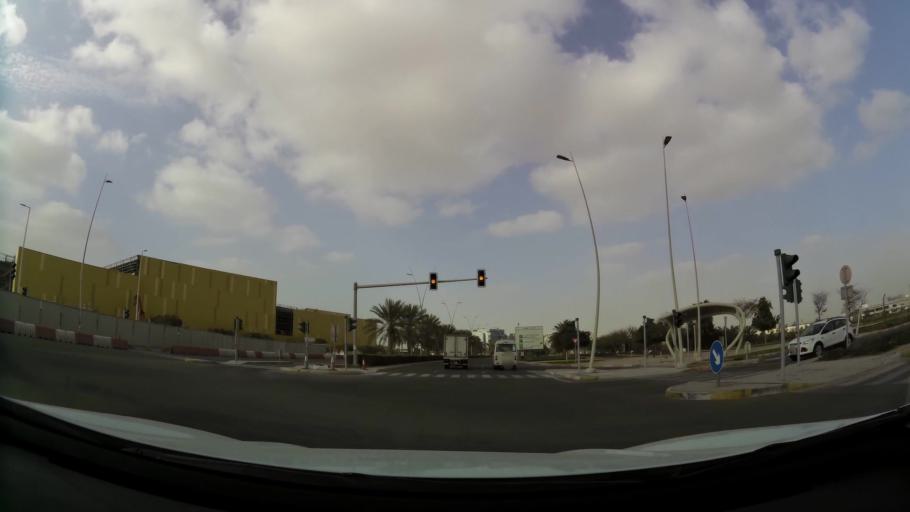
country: AE
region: Abu Dhabi
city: Abu Dhabi
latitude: 24.4892
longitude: 54.6022
